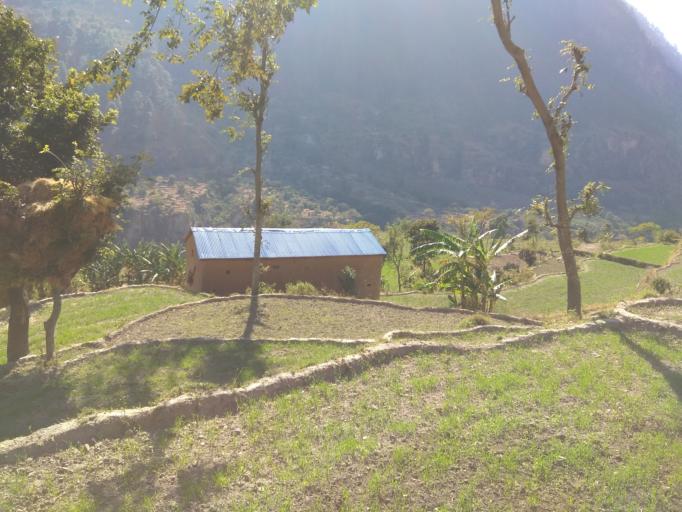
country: NP
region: Mid Western
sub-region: Bheri Zone
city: Dailekh
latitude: 29.2235
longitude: 81.6446
